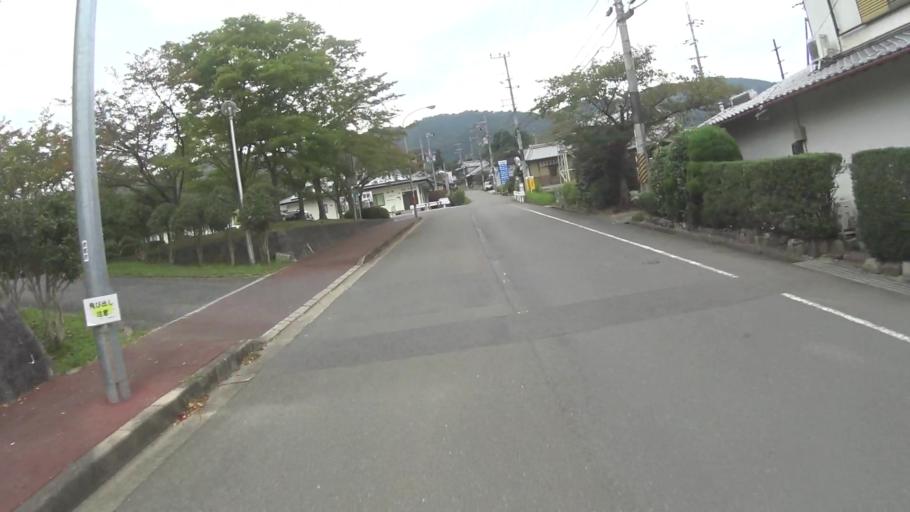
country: JP
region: Kyoto
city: Uji
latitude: 34.7960
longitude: 135.8960
